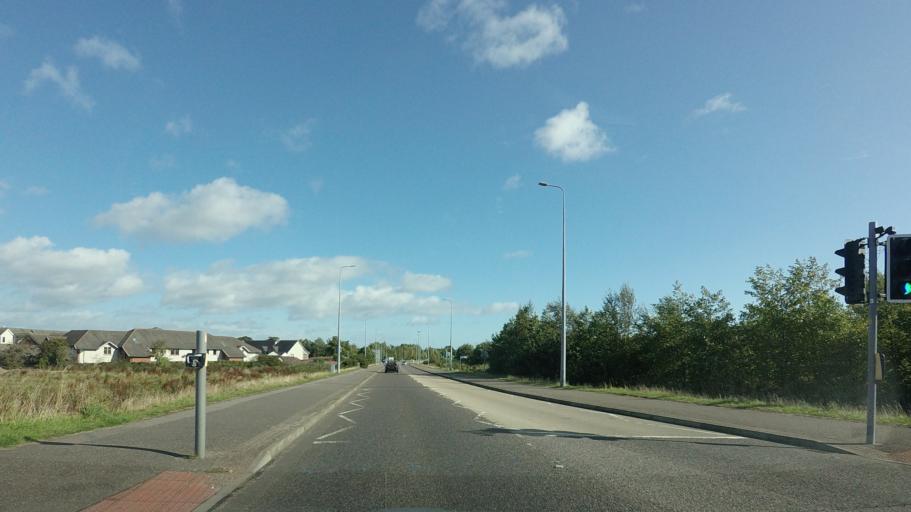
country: GB
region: Scotland
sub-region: Highland
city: Inverness
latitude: 57.4506
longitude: -4.2180
